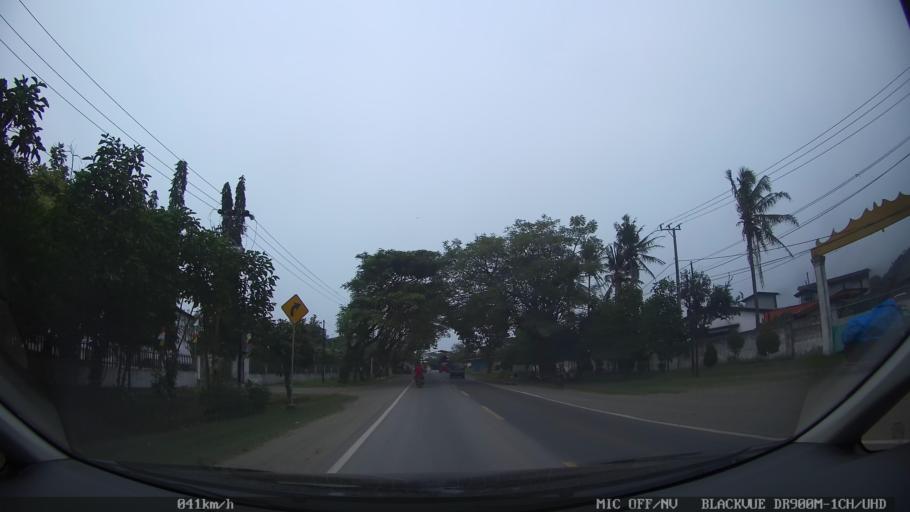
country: ID
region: Lampung
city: Panjang
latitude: -5.4346
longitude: 105.3243
